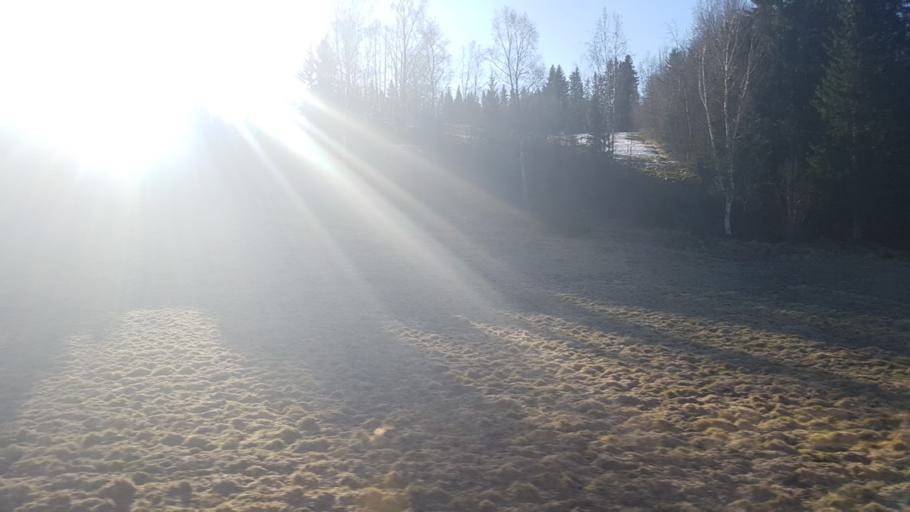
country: NO
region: Nord-Trondelag
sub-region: Levanger
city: Skogn
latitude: 63.6659
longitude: 11.1052
